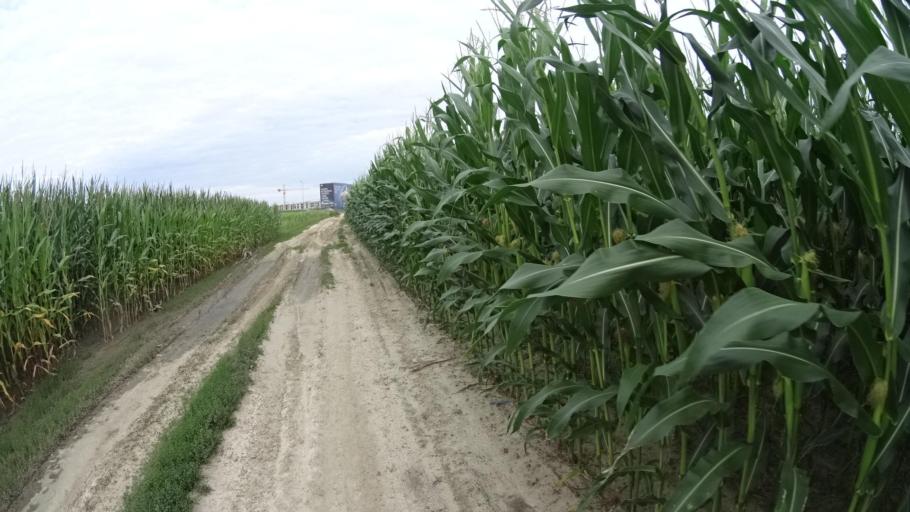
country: PL
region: Masovian Voivodeship
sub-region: Powiat warszawski zachodni
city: Babice
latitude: 52.2323
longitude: 20.8783
